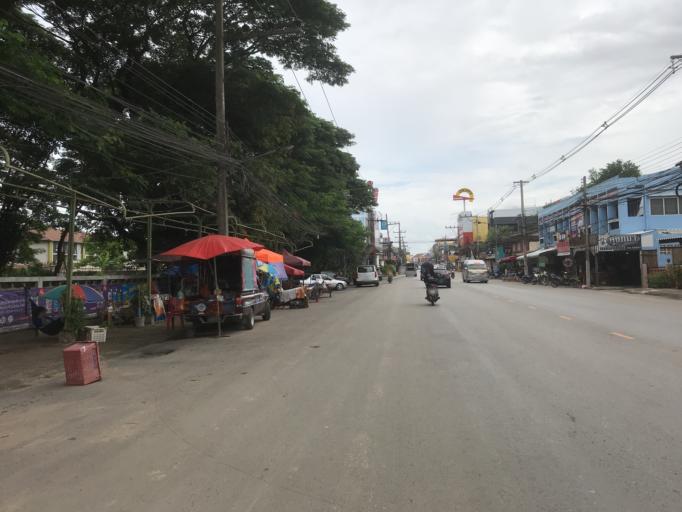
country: TH
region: Chiang Rai
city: Chiang Rai
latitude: 19.8934
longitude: 99.8311
